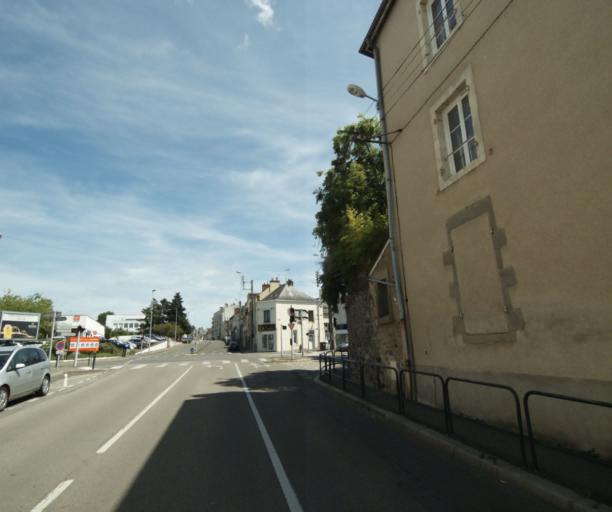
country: FR
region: Pays de la Loire
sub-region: Departement de la Mayenne
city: Laval
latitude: 48.0671
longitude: -0.7622
